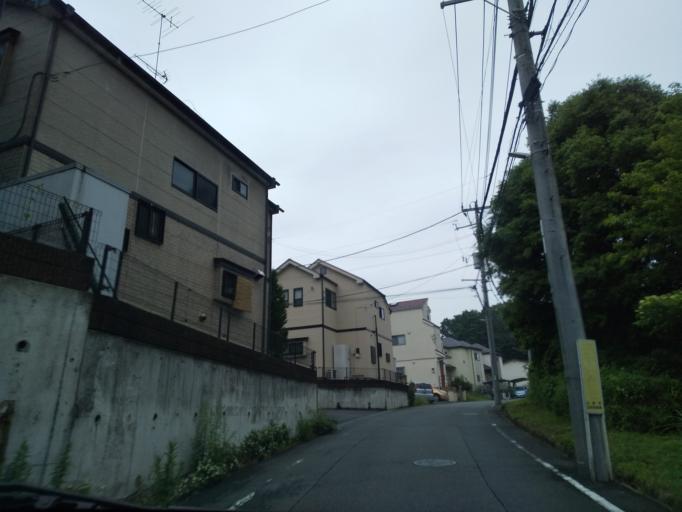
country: JP
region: Tokyo
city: Hino
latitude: 35.6471
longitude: 139.4297
